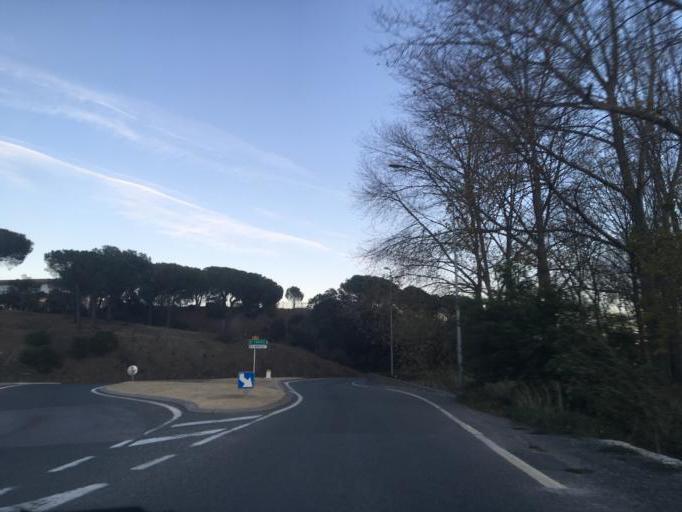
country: FR
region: Provence-Alpes-Cote d'Azur
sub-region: Departement du Var
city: Sainte-Maxime
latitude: 43.3277
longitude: 6.6137
